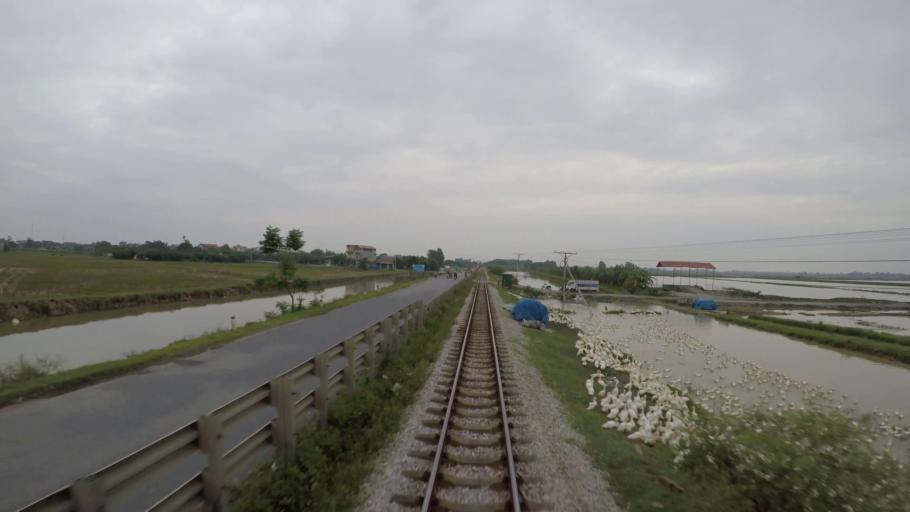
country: VN
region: Hung Yen
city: Ban Yen Nhan
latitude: 20.9845
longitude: 106.0716
